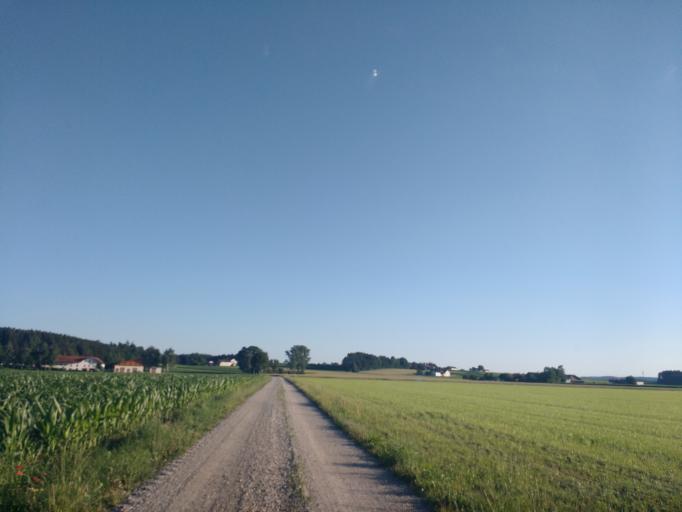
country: DE
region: Bavaria
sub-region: Upper Bavaria
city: Taufkirchen
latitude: 48.1389
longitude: 12.4694
